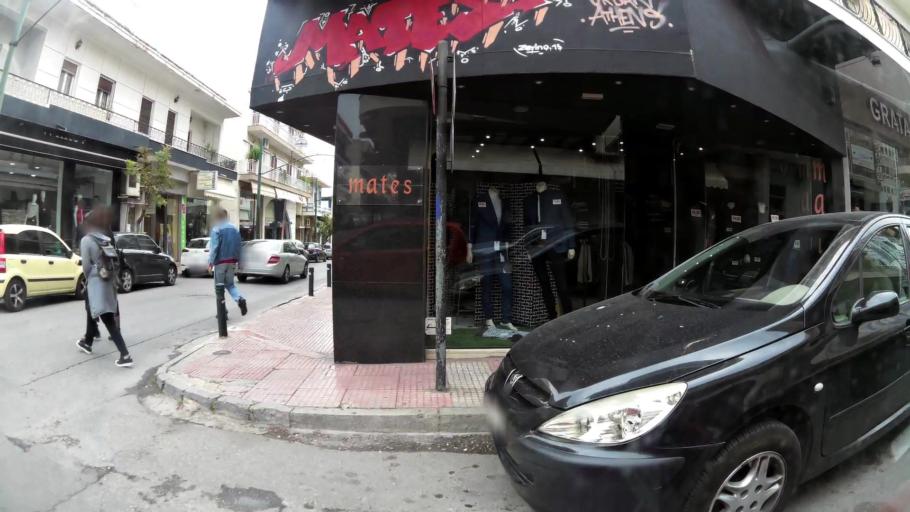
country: GR
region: Attica
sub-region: Nomarchia Athinas
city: Ilion
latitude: 38.0326
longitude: 23.7066
